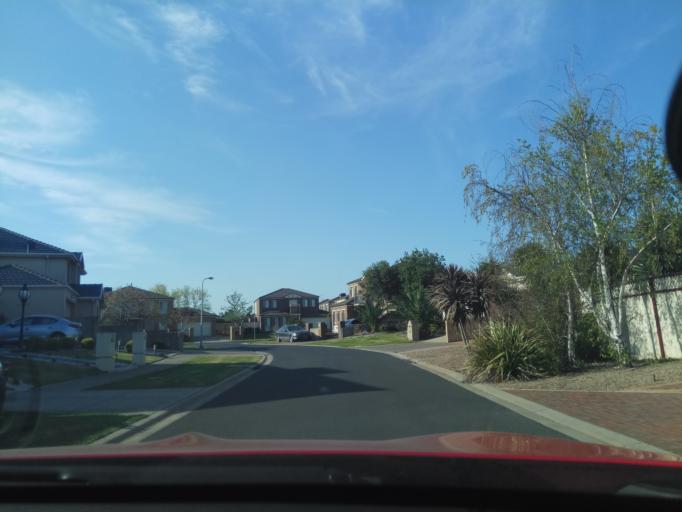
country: AU
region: Victoria
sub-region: Hobsons Bay
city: Altona Meadows
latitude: -37.8828
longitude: 144.7700
